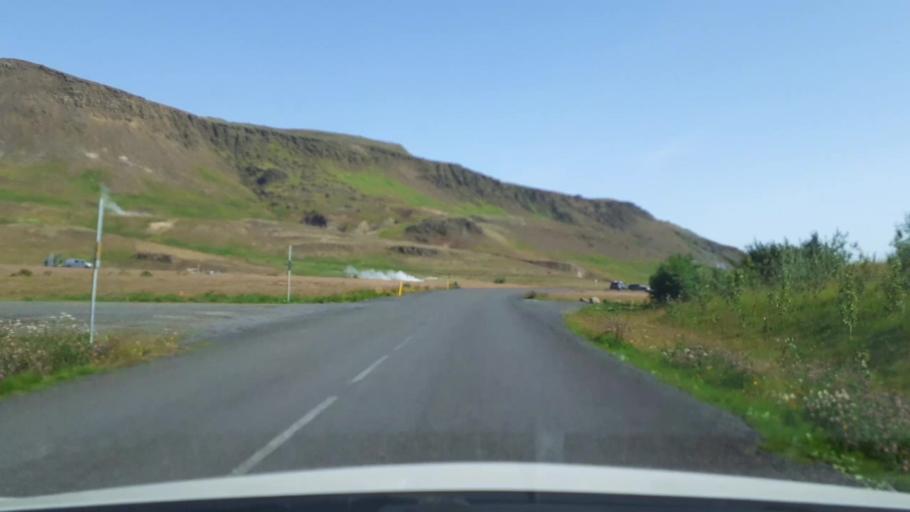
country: IS
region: South
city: Hveragerdi
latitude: 64.0126
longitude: -21.1940
